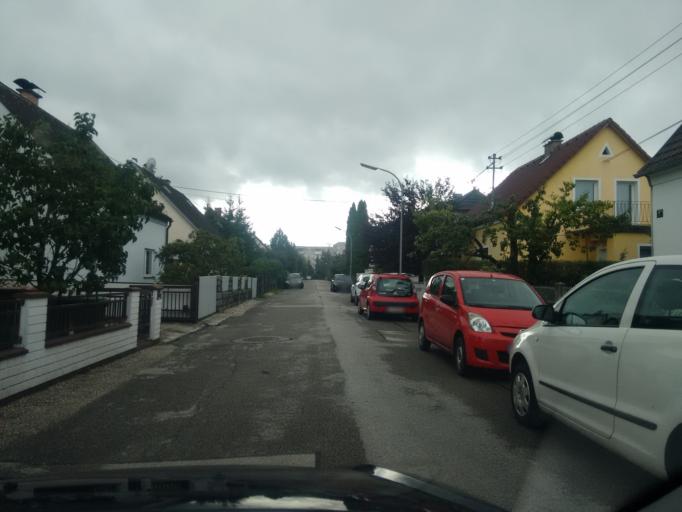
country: AT
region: Upper Austria
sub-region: Politischer Bezirk Linz-Land
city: Traun
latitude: 48.2303
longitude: 14.2486
